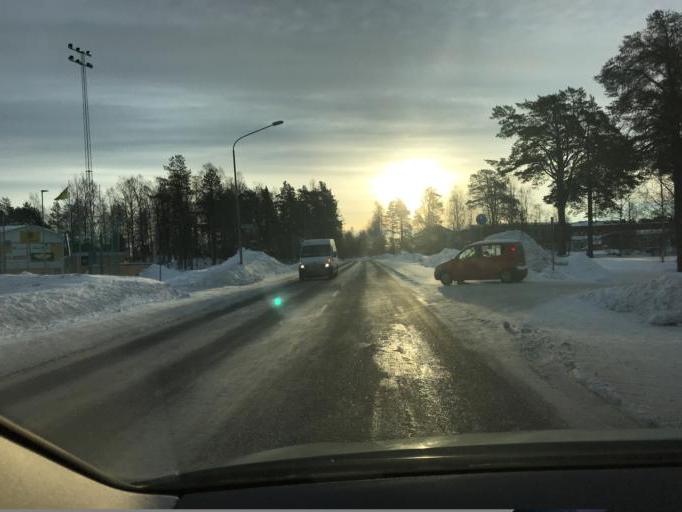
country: SE
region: Norrbotten
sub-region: Lulea Kommun
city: Bergnaset
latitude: 65.6068
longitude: 22.1092
